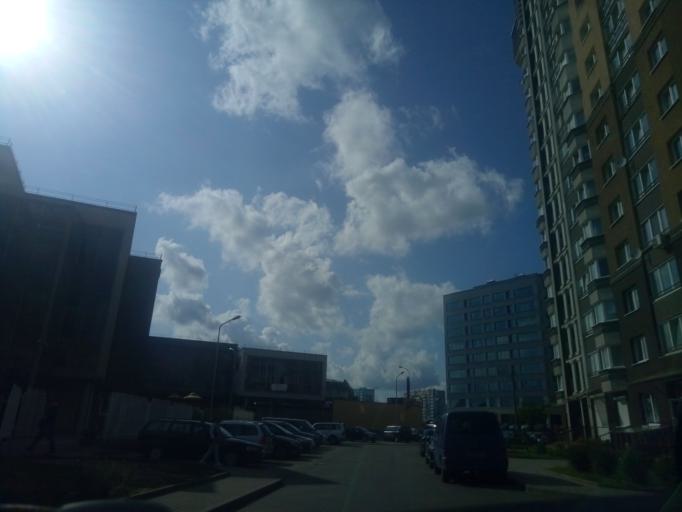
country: BY
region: Minsk
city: Novoye Medvezhino
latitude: 53.9049
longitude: 27.4584
